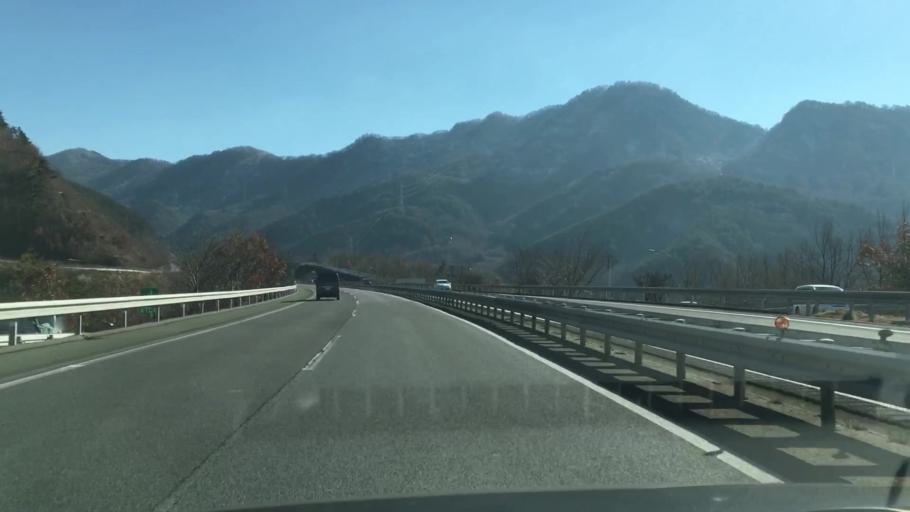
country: JP
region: Nagano
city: Ueda
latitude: 36.4464
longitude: 138.2057
